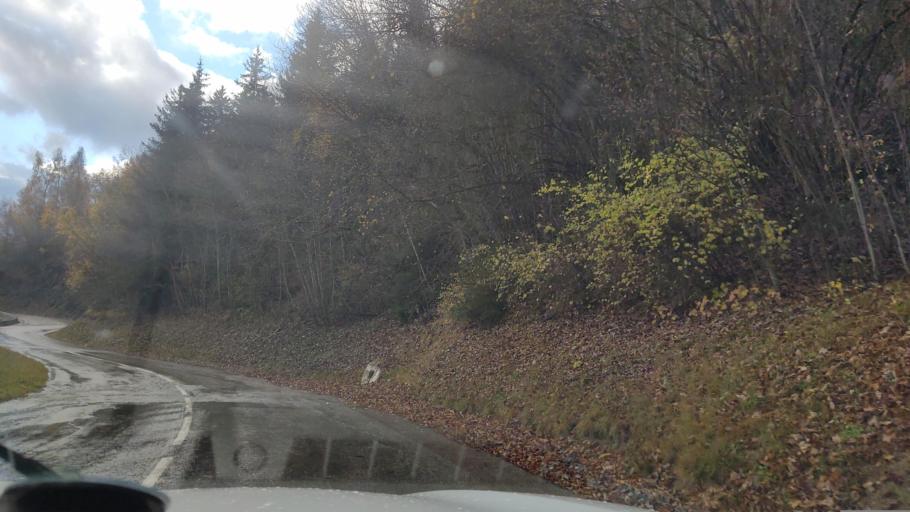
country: FR
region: Rhone-Alpes
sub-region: Departement de la Savoie
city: Saint-Jean-de-Maurienne
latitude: 45.2628
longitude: 6.3027
